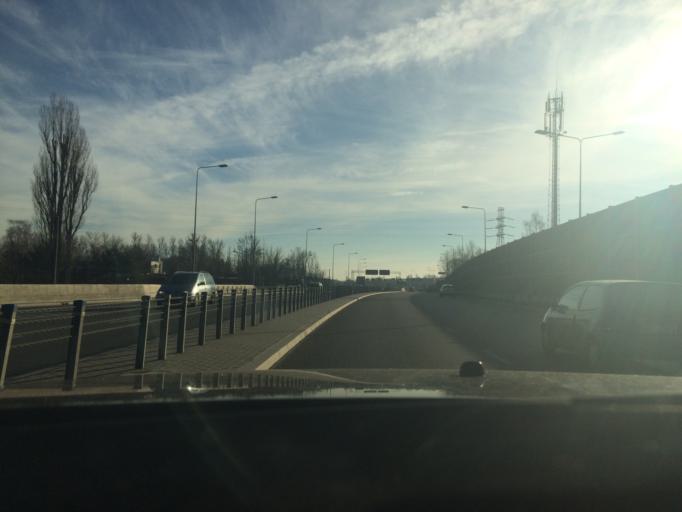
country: PL
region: Lodz Voivodeship
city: Lodz
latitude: 51.7206
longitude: 19.4550
